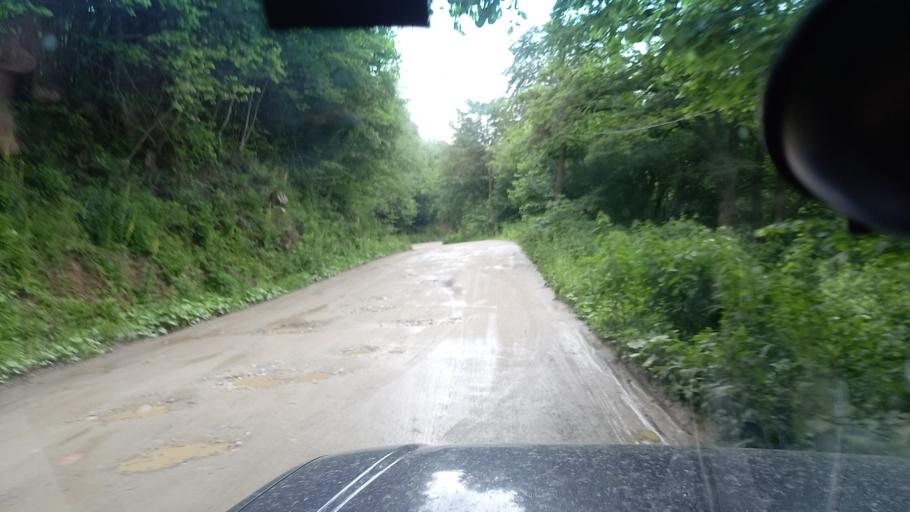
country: RU
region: Krasnodarskiy
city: Psebay
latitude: 44.0273
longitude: 40.7330
